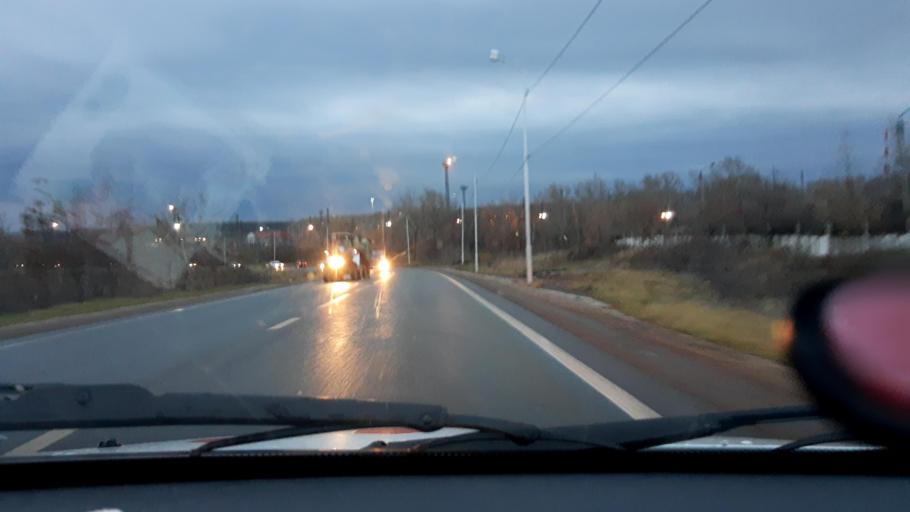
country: RU
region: Bashkortostan
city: Ufa
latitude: 54.8413
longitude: 56.1232
